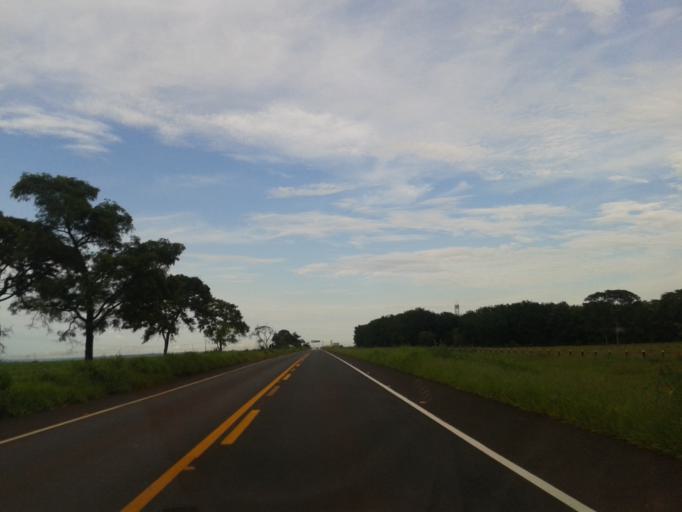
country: BR
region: Minas Gerais
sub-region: Santa Vitoria
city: Santa Vitoria
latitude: -19.0420
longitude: -50.4247
